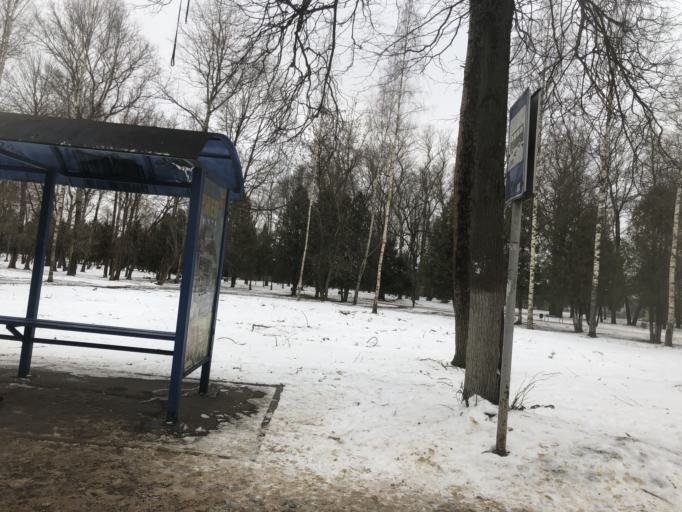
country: RU
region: Tverskaya
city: Rzhev
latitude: 56.2626
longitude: 34.3350
